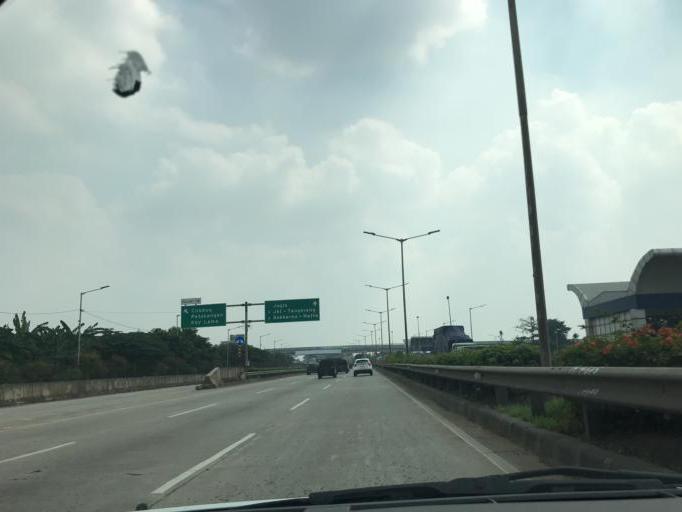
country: ID
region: Banten
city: South Tangerang
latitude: -6.2412
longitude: 106.7585
